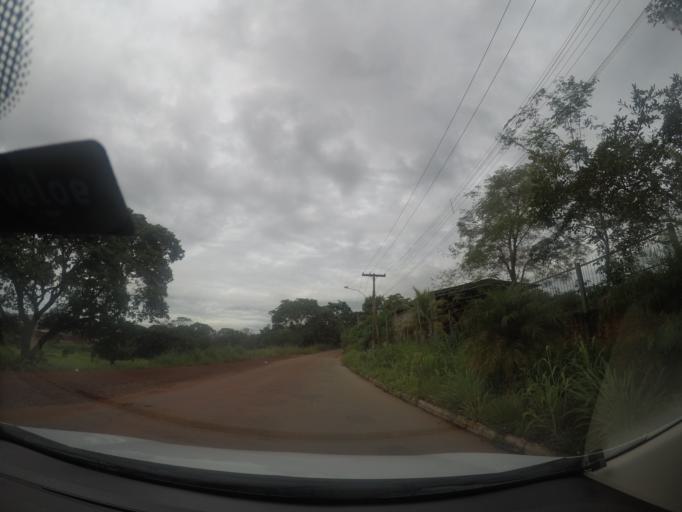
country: BR
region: Goias
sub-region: Goiania
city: Goiania
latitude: -16.6378
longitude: -49.3323
